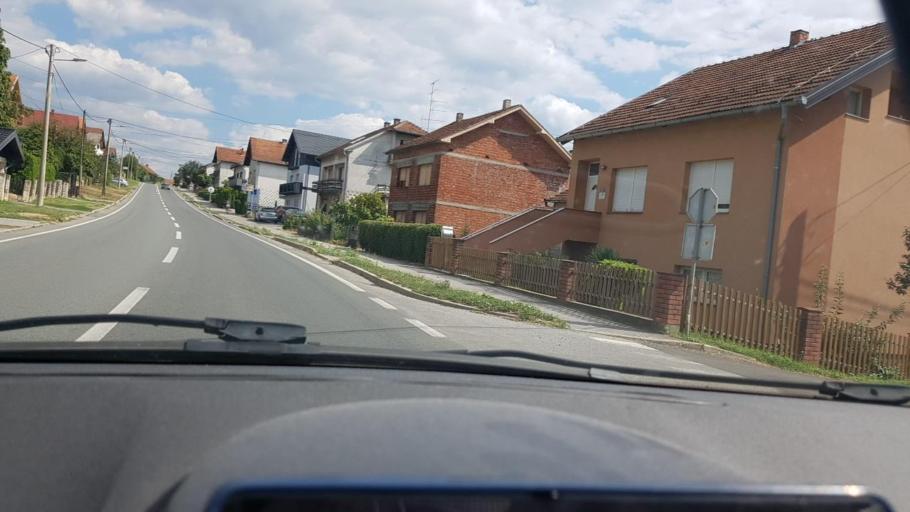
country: HR
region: Bjelovarsko-Bilogorska
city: Zdralovi
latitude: 45.8804
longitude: 16.8687
